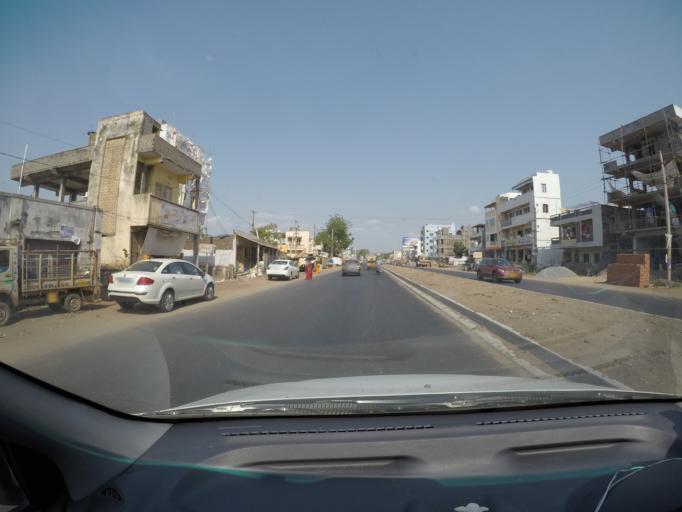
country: IN
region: Andhra Pradesh
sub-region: Krishna
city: Yanamalakuduru
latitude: 16.4772
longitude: 80.7044
